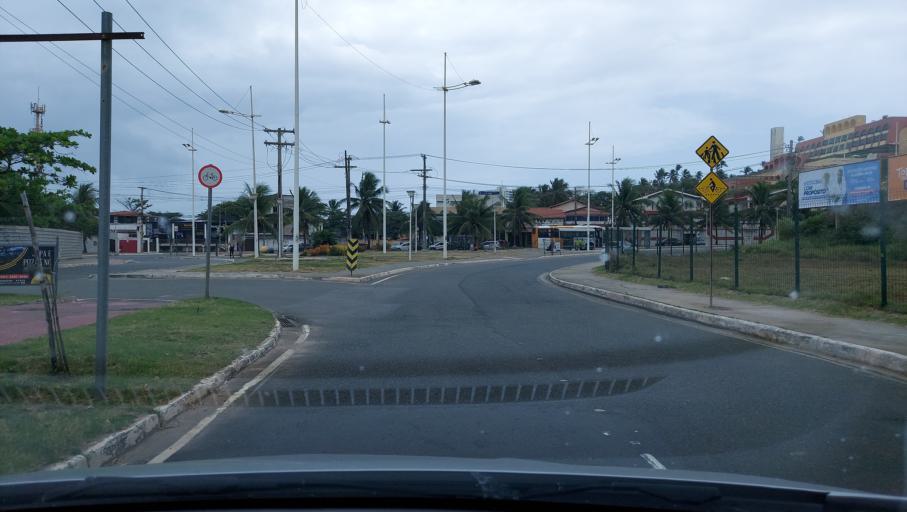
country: BR
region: Bahia
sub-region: Lauro De Freitas
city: Lauro de Freitas
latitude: -12.9618
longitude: -38.4033
